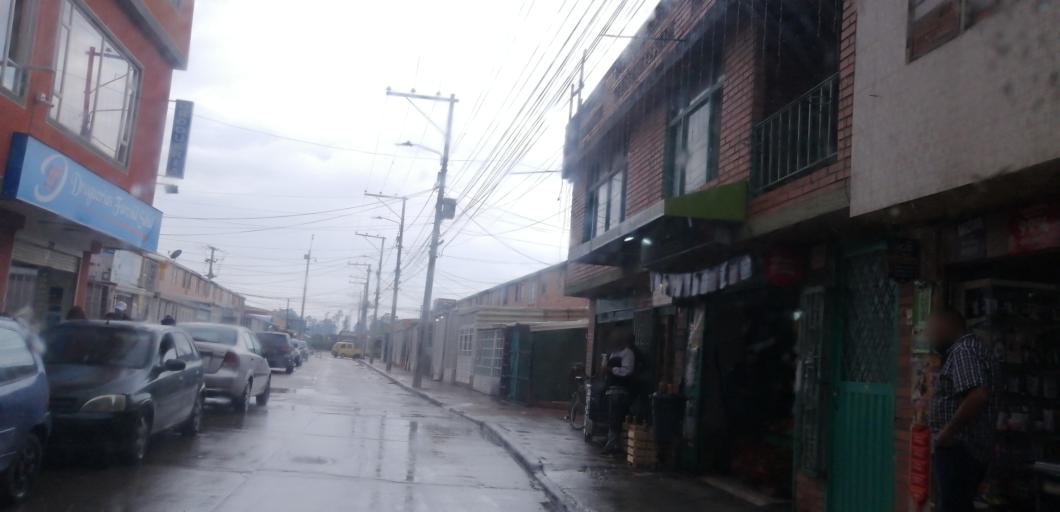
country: CO
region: Cundinamarca
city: Madrid
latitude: 4.7262
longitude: -74.2835
